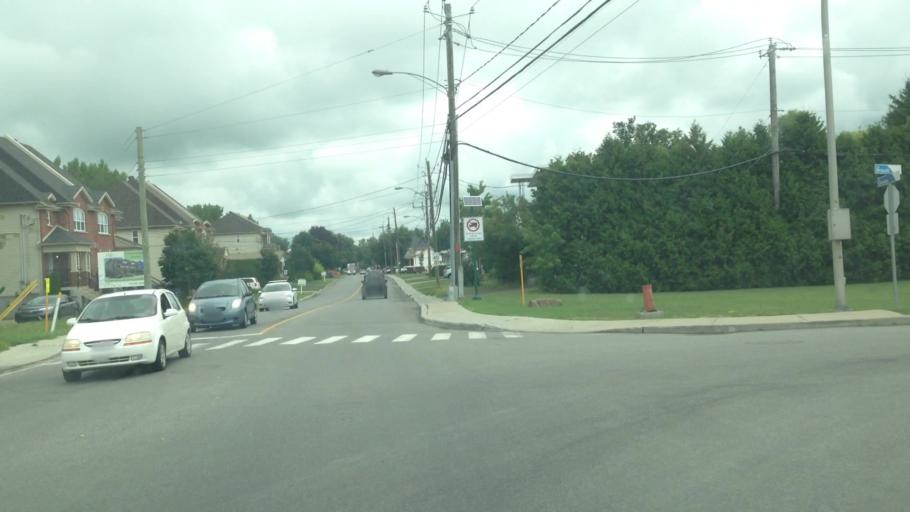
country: CA
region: Quebec
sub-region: Laurentides
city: Blainville
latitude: 45.6974
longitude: -73.9314
